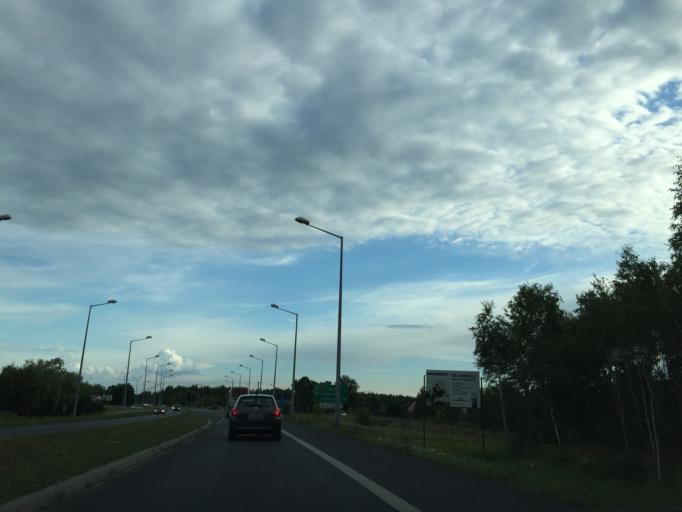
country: PL
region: Lublin Voivodeship
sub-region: Powiat lubartowski
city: Lubartow
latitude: 51.4649
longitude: 22.5778
